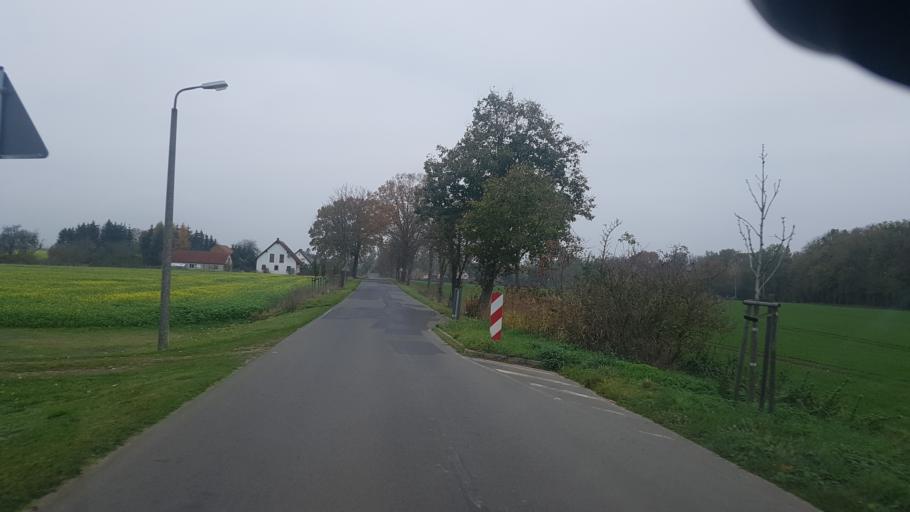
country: DE
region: Brandenburg
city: Schonermark
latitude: 52.9138
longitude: 13.1330
